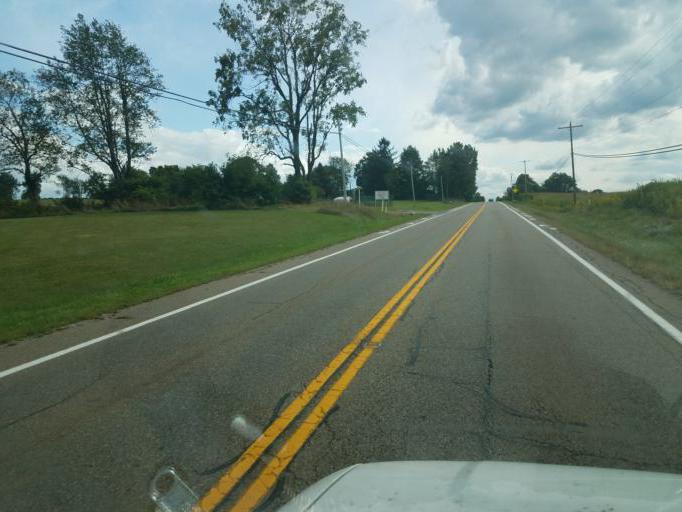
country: US
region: Ohio
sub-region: Portage County
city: Ravenna
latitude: 41.0483
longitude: -81.2479
